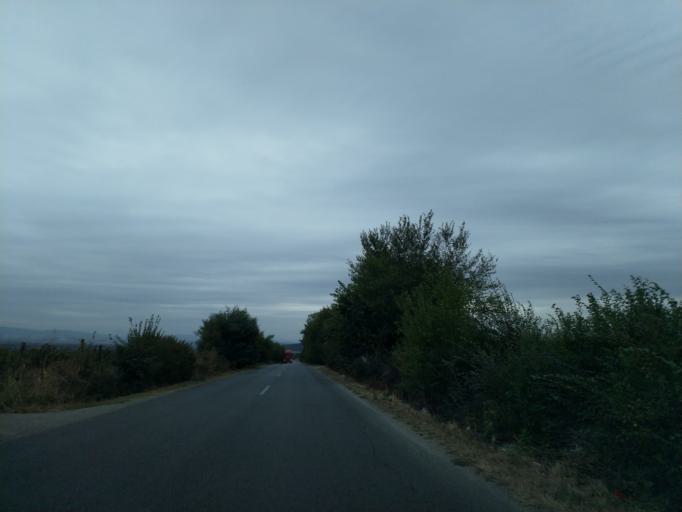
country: RS
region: Central Serbia
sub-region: Pomoravski Okrug
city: Jagodina
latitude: 43.9969
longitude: 21.2196
